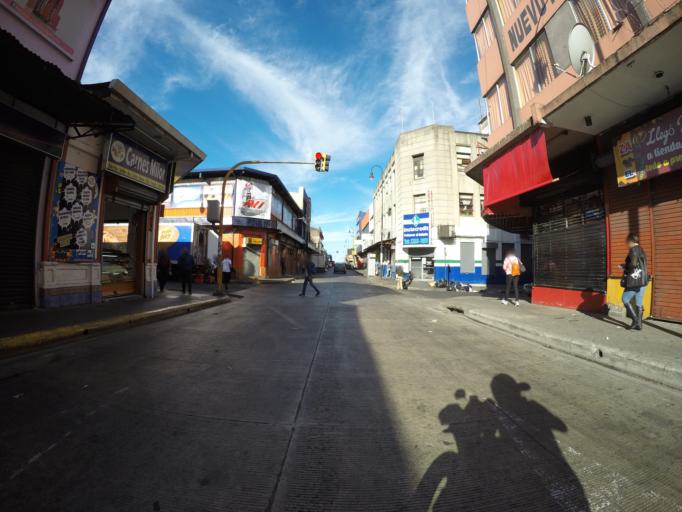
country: CR
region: San Jose
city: San Jose
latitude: 9.9359
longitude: -84.0813
